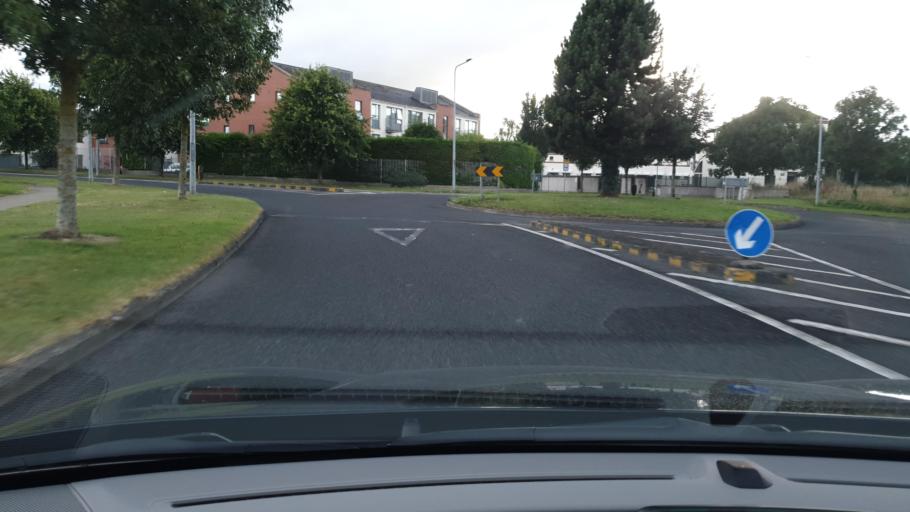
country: IE
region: Leinster
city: Clondalkin
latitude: 53.3296
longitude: -6.4231
